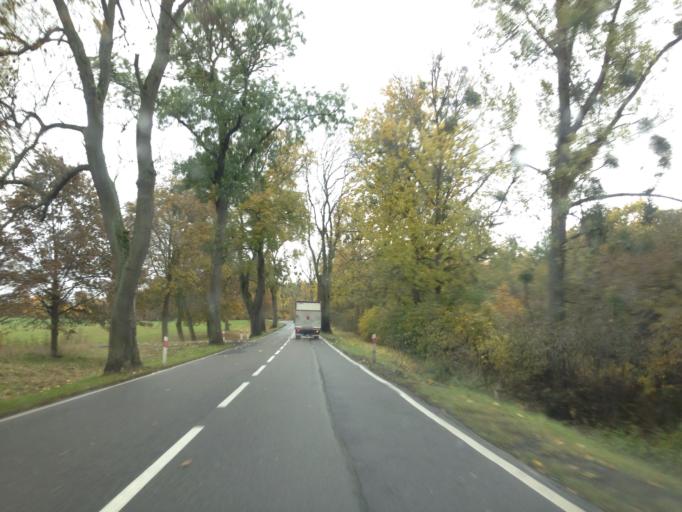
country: PL
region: Pomeranian Voivodeship
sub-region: Powiat kwidzynski
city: Ryjewo
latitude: 53.8522
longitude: 18.9992
